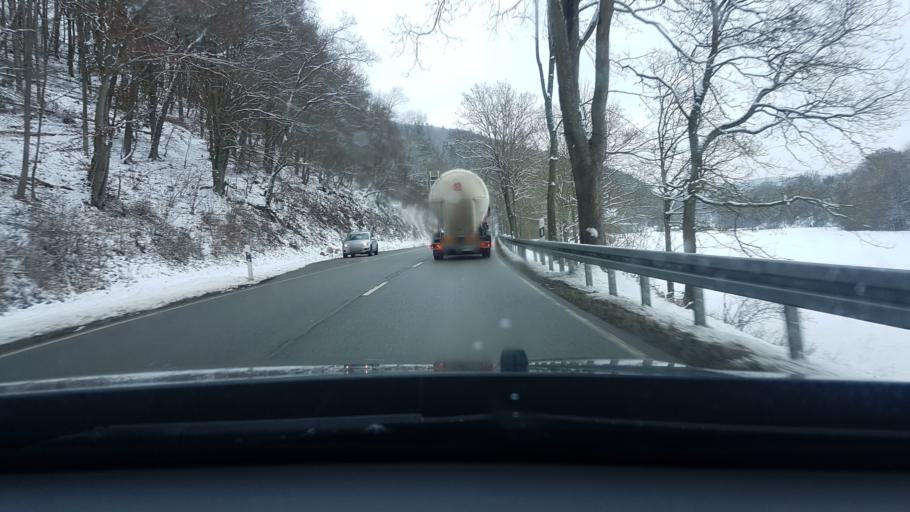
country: DE
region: North Rhine-Westphalia
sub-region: Regierungsbezirk Arnsberg
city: Medebach
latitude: 51.2912
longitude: 8.7460
